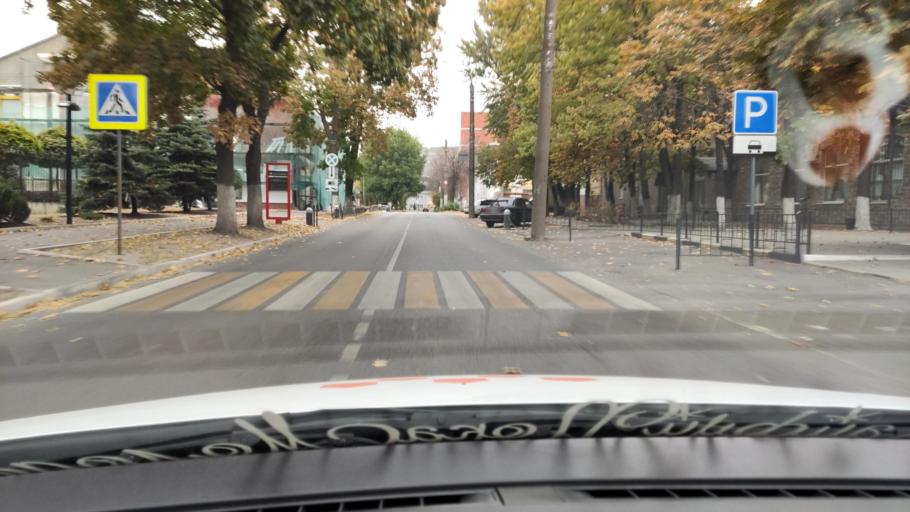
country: RU
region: Voronezj
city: Voronezh
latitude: 51.6853
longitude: 39.1700
